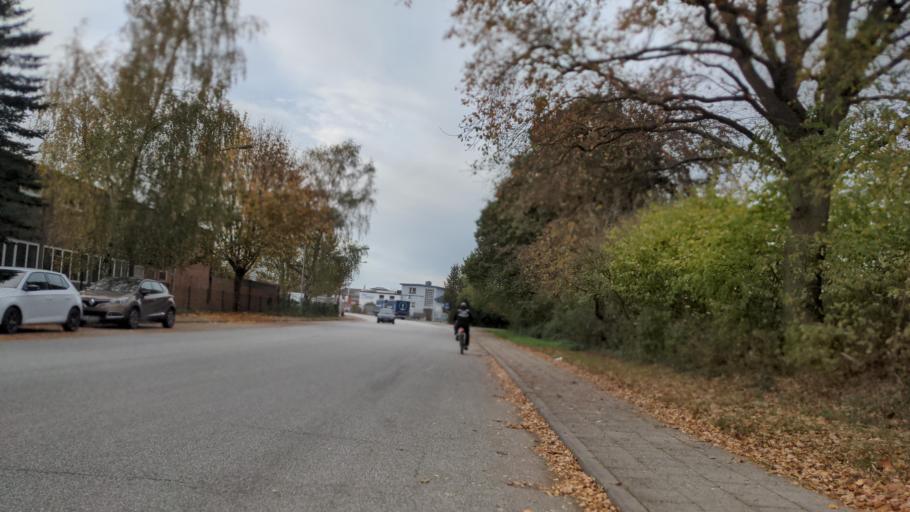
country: DE
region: Schleswig-Holstein
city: Stockelsdorf
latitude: 53.8579
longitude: 10.6402
